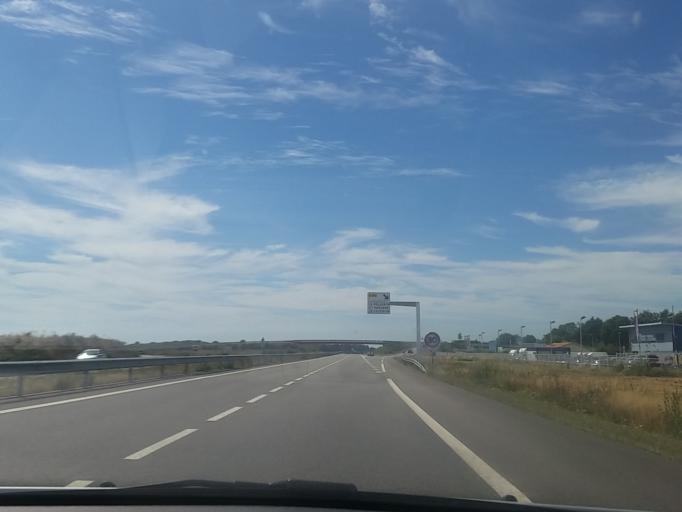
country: FR
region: Pays de la Loire
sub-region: Departement de la Loire-Atlantique
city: Le Pellerin
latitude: 47.1843
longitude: -1.7733
